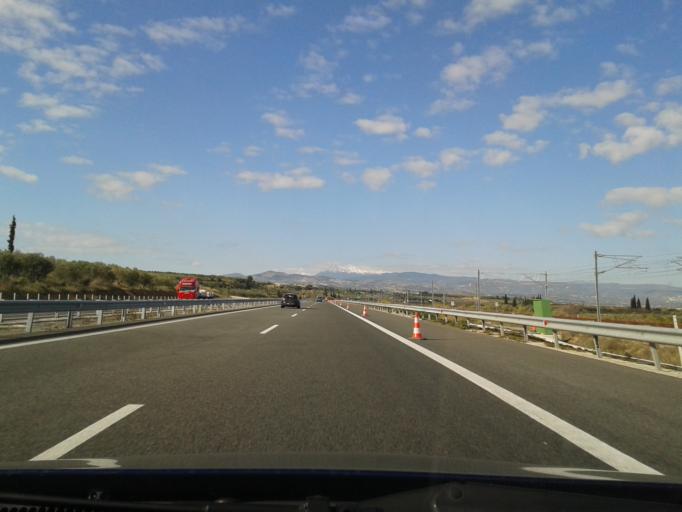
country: GR
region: Peloponnese
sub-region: Nomos Korinthias
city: Lekhaio
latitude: 37.9089
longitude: 22.8530
